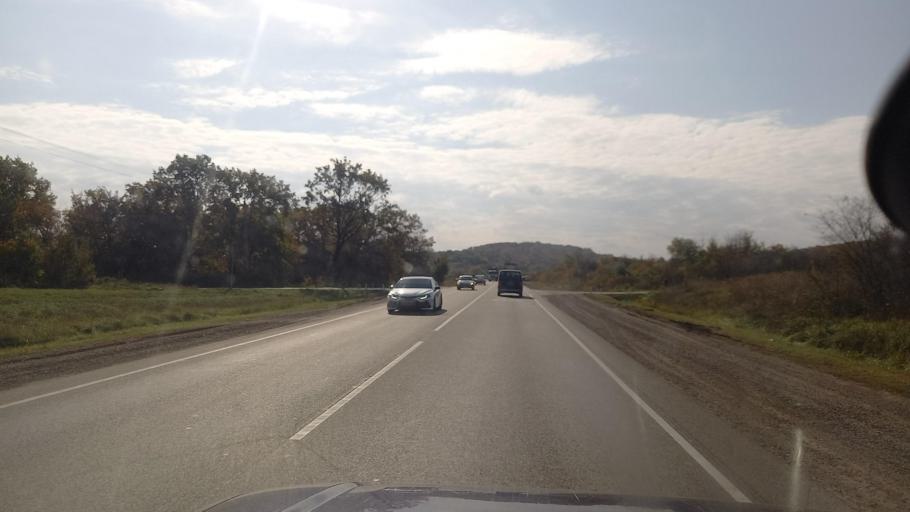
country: RU
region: Krasnodarskiy
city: Abinsk
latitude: 44.8553
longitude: 38.1337
